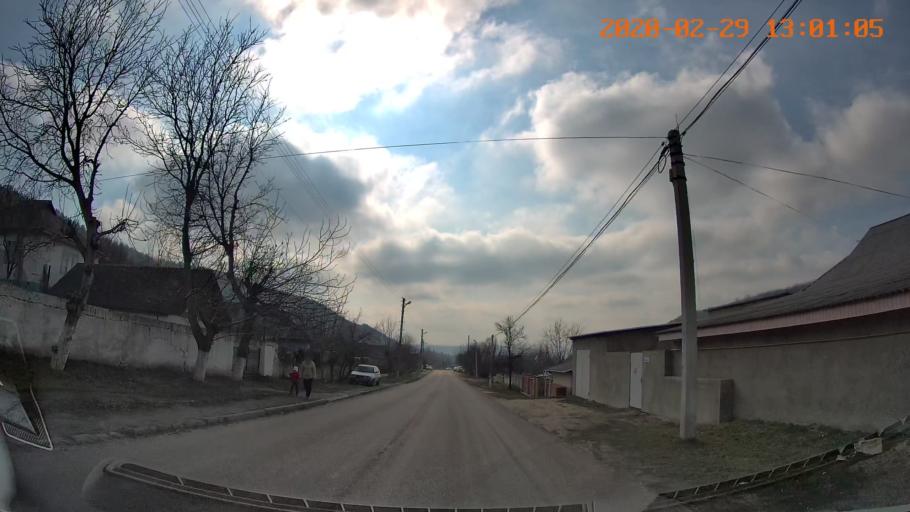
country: MD
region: Telenesti
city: Camenca
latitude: 48.0469
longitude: 28.7204
